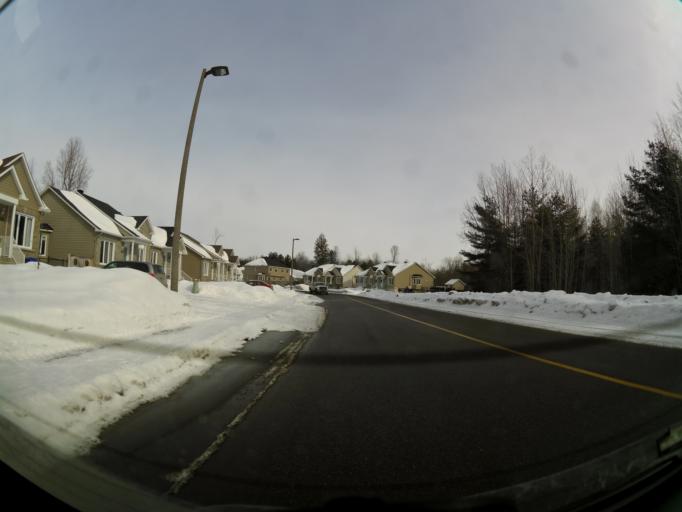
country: CA
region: Quebec
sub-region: Outaouais
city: Gatineau
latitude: 45.5068
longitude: -75.5728
